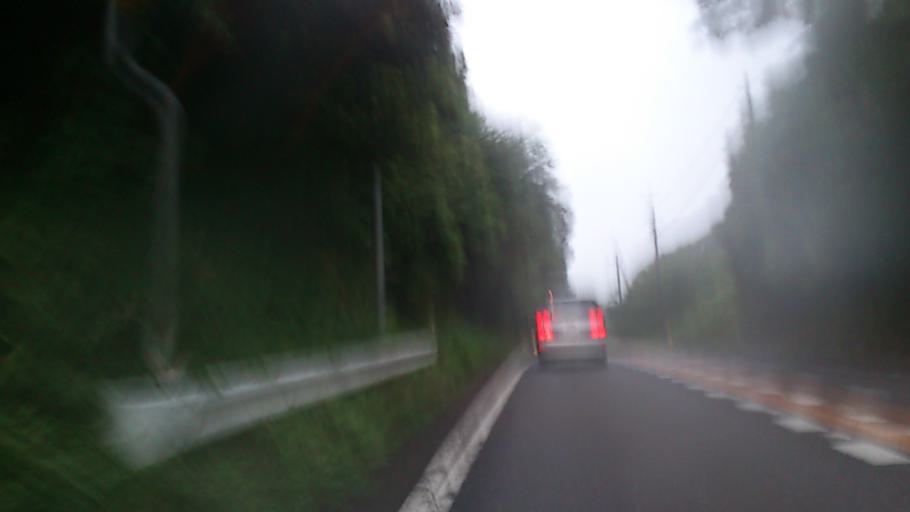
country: JP
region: Tochigi
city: Kuroiso
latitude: 37.0992
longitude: 140.1382
